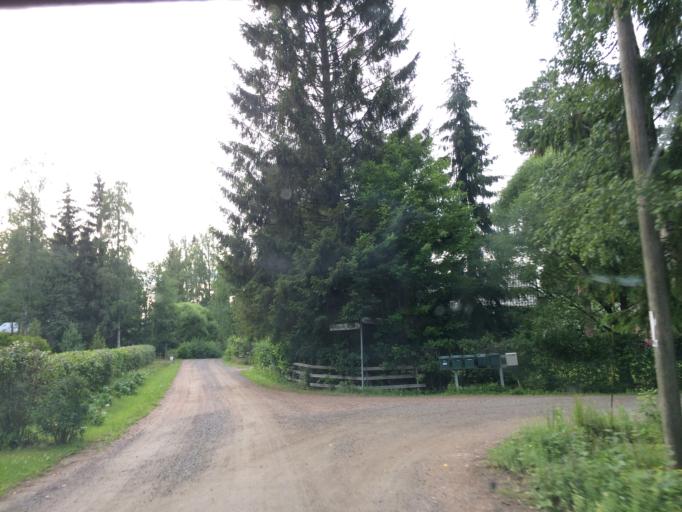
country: FI
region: Haeme
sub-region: Haemeenlinna
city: Tervakoski
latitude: 60.8547
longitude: 24.6238
